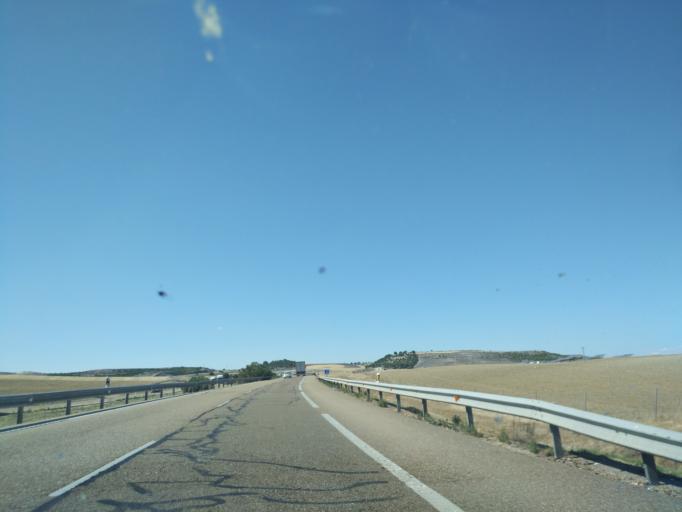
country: ES
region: Castille and Leon
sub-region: Provincia de Valladolid
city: Mota del Marques
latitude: 41.6519
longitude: -5.1915
